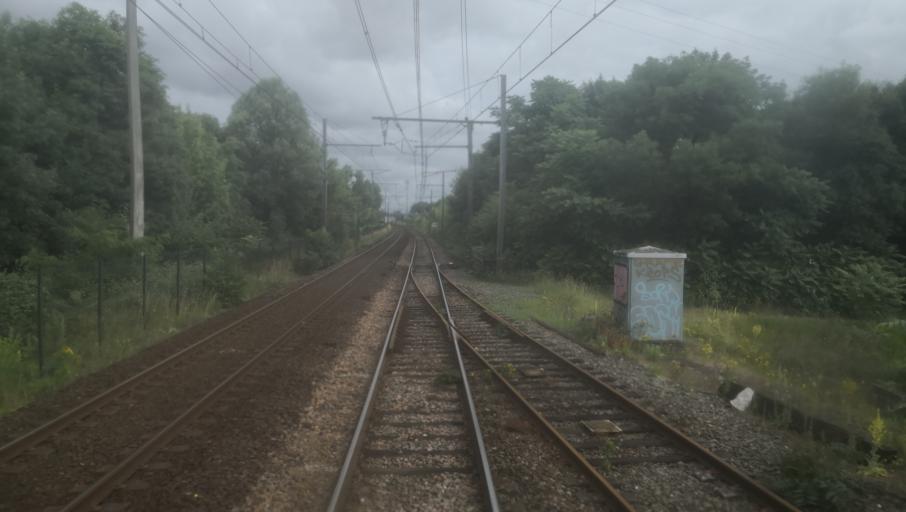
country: FR
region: Aquitaine
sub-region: Departement de la Gironde
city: Begles
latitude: 44.7929
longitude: -0.5533
